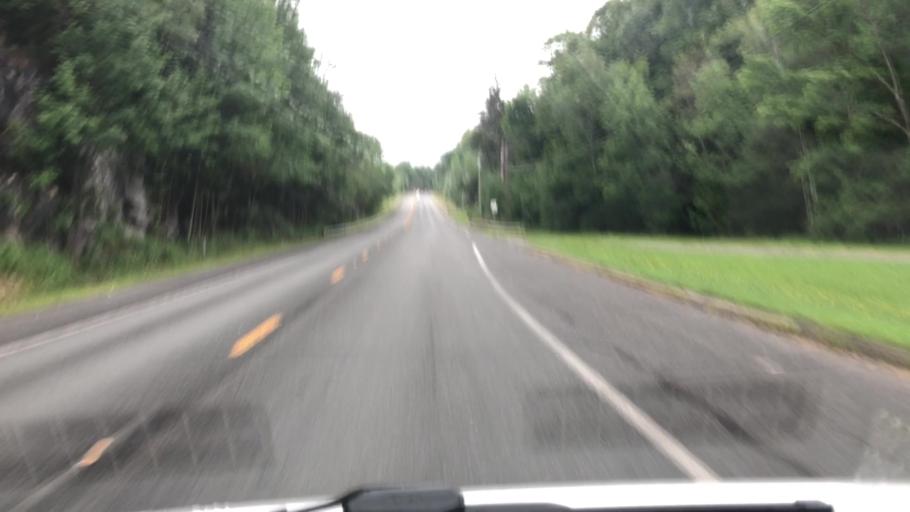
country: US
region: Massachusetts
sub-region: Berkshire County
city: Lanesborough
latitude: 42.5997
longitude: -73.2414
